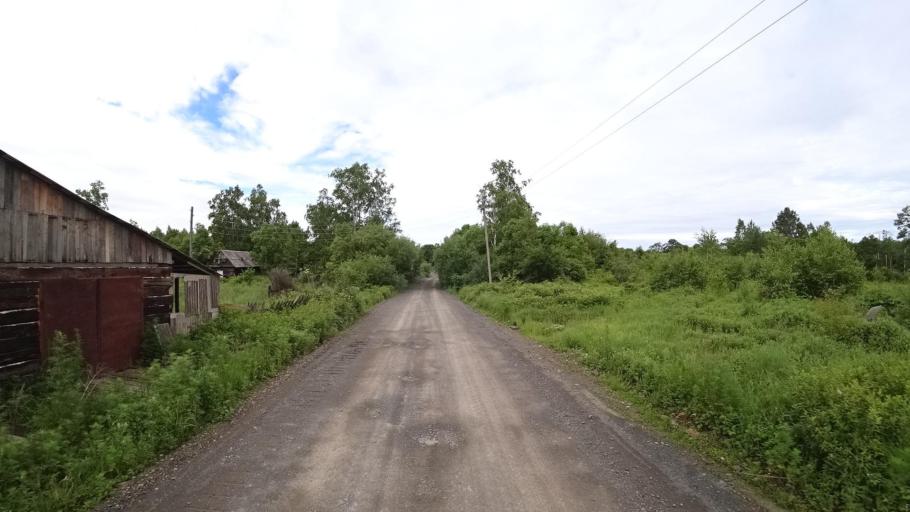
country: RU
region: Khabarovsk Krai
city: Amursk
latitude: 49.8975
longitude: 136.1298
